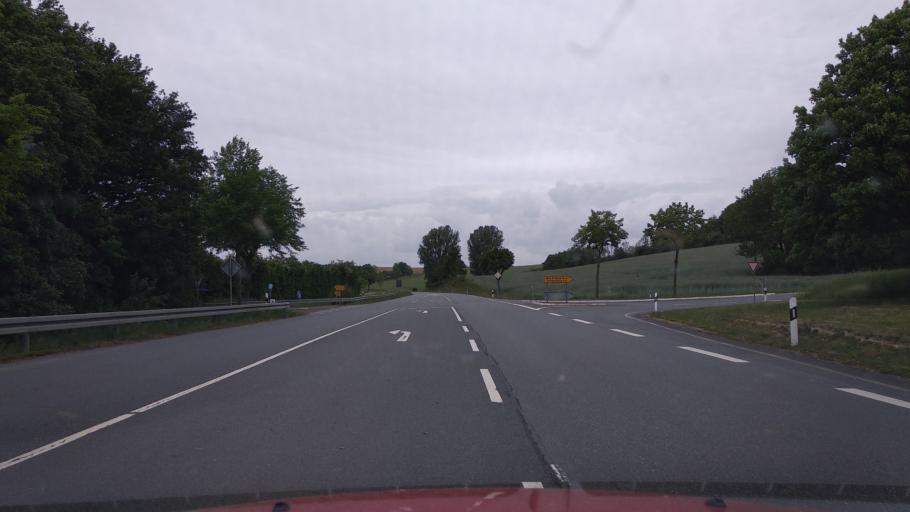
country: DE
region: North Rhine-Westphalia
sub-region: Regierungsbezirk Detmold
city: Willebadessen
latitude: 51.6293
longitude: 9.0808
